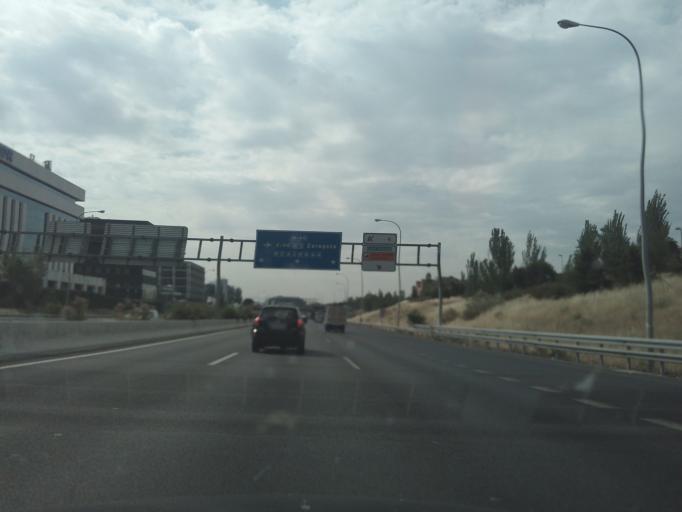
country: ES
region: Madrid
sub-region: Provincia de Madrid
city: Hortaleza
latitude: 40.4661
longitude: -3.6262
